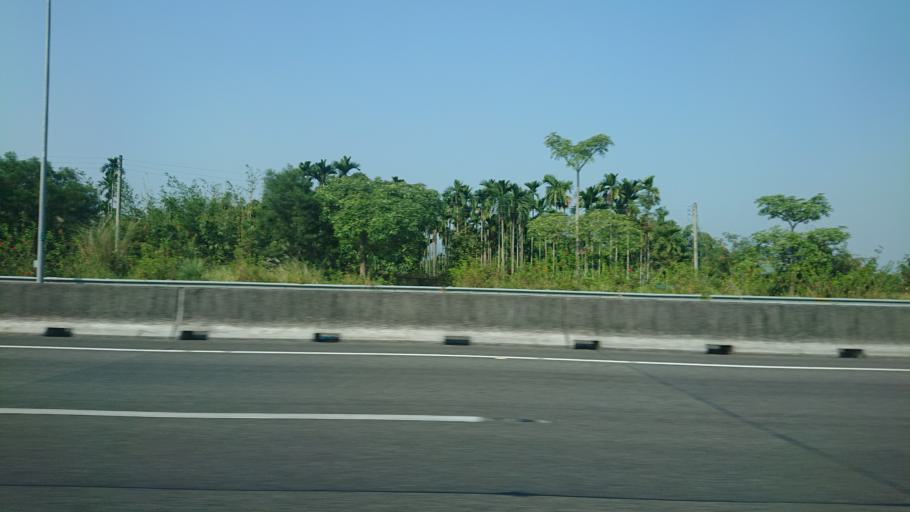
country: TW
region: Taiwan
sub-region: Nantou
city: Nantou
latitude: 23.8726
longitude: 120.7058
